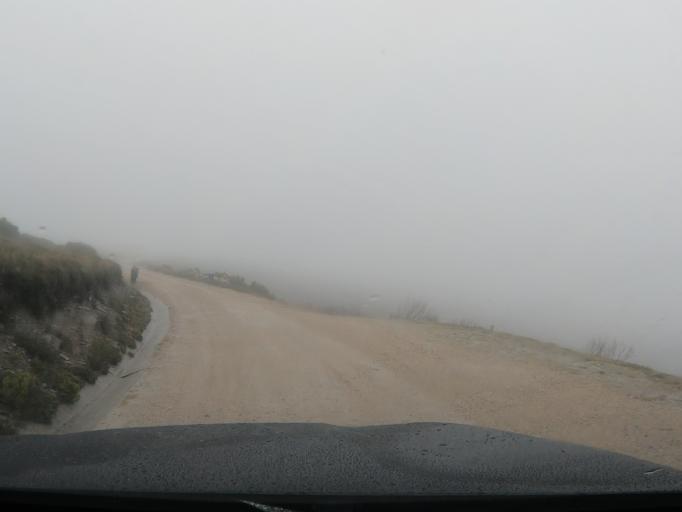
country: PT
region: Vila Real
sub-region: Vila Real
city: Vila Real
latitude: 41.3300
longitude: -7.8347
